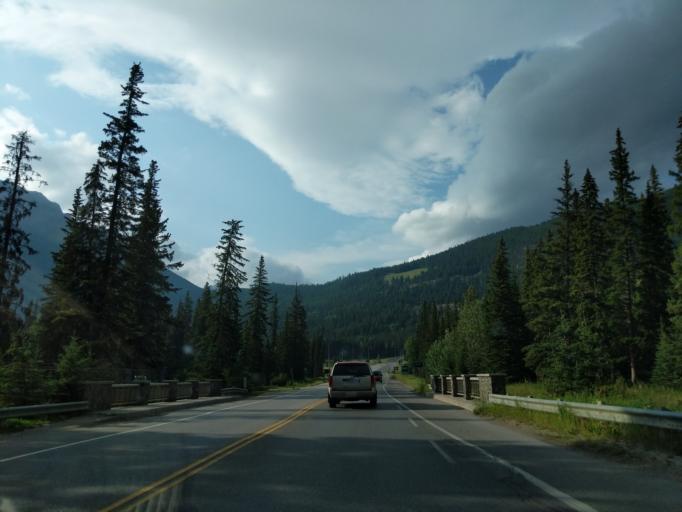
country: CA
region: Alberta
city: Banff
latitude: 51.1836
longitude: -115.5808
